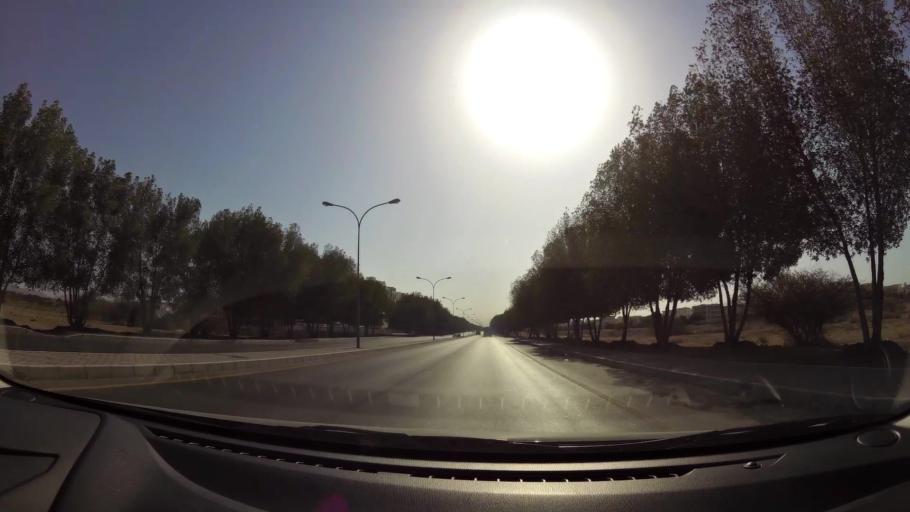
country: OM
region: Muhafazat Masqat
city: As Sib al Jadidah
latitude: 23.6154
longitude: 58.2080
